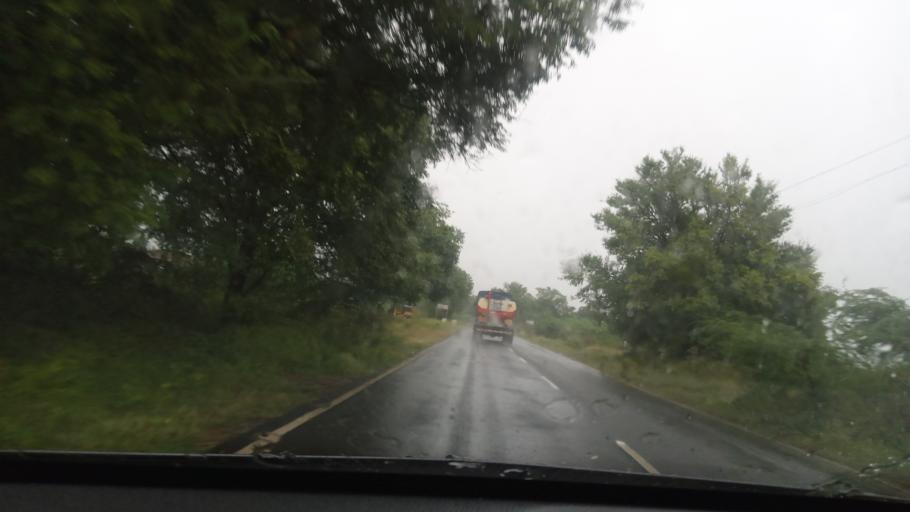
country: IN
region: Tamil Nadu
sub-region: Vellore
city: Kalavai
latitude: 12.8172
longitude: 79.4113
